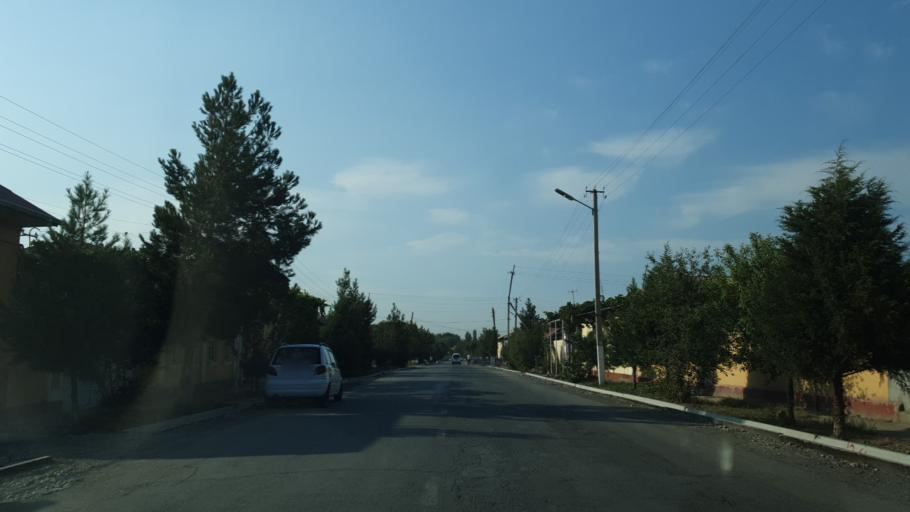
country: UZ
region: Fergana
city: Yaypan
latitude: 40.3724
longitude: 70.8130
